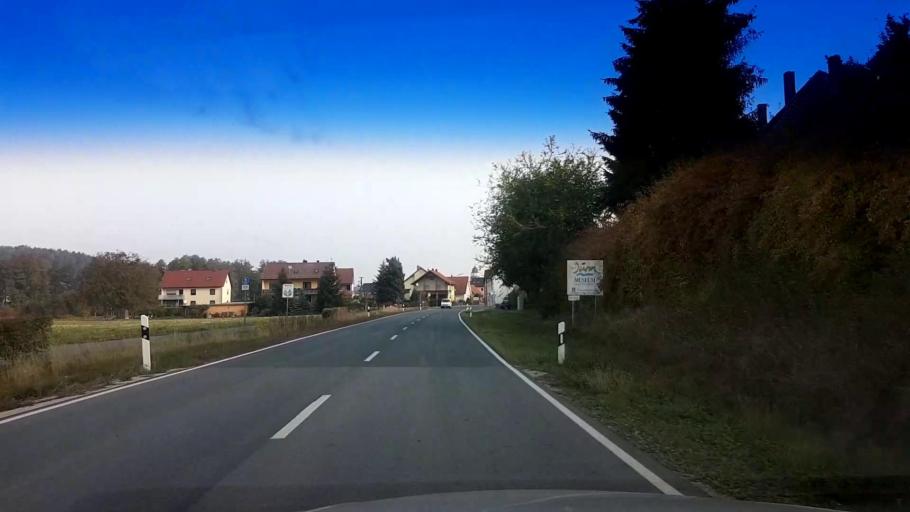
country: DE
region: Bavaria
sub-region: Upper Franconia
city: Weismain
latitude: 50.0796
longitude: 11.2341
